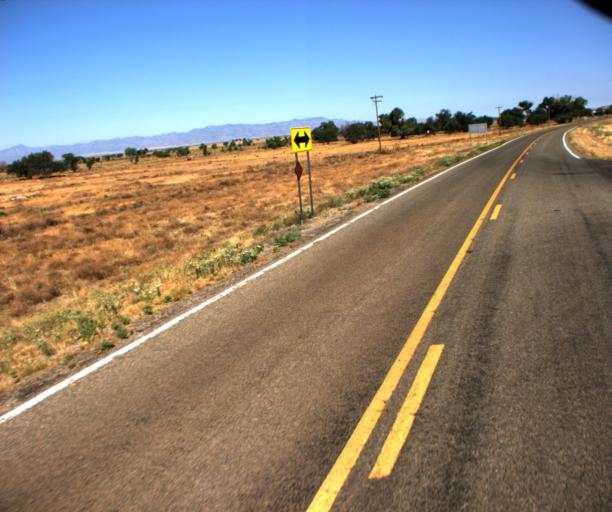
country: US
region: Arizona
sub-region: Graham County
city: Swift Trail Junction
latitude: 32.5842
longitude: -109.9605
